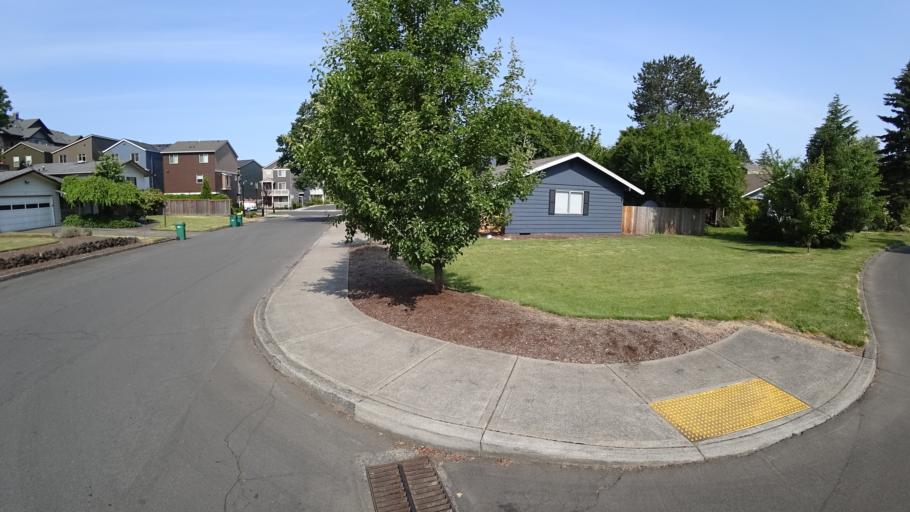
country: US
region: Oregon
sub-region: Washington County
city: Cedar Hills
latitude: 45.5041
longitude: -122.8211
